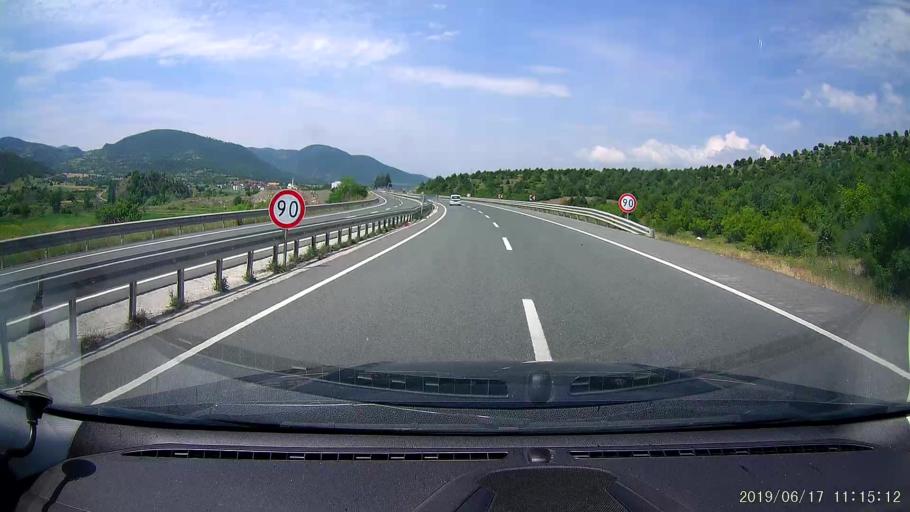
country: TR
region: Kastamonu
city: Tosya
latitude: 40.9533
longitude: 33.9281
